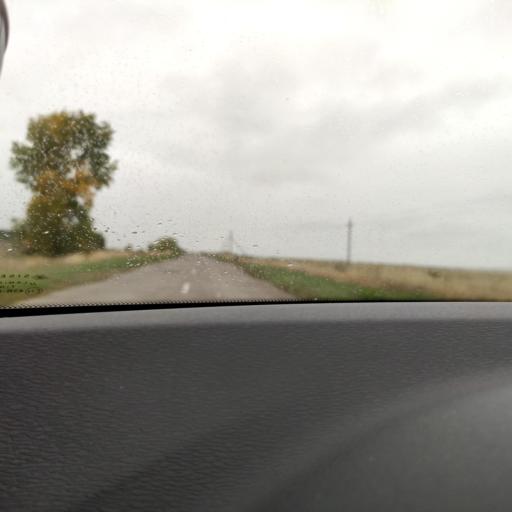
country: RU
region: Samara
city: Yelkhovka
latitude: 53.7143
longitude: 50.3253
